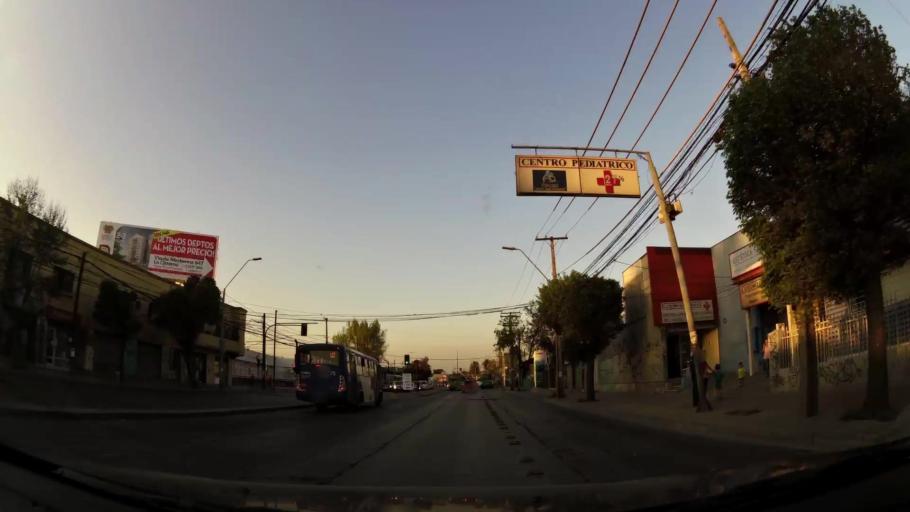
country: CL
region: Santiago Metropolitan
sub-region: Provincia de Santiago
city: La Pintana
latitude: -33.5439
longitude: -70.6669
